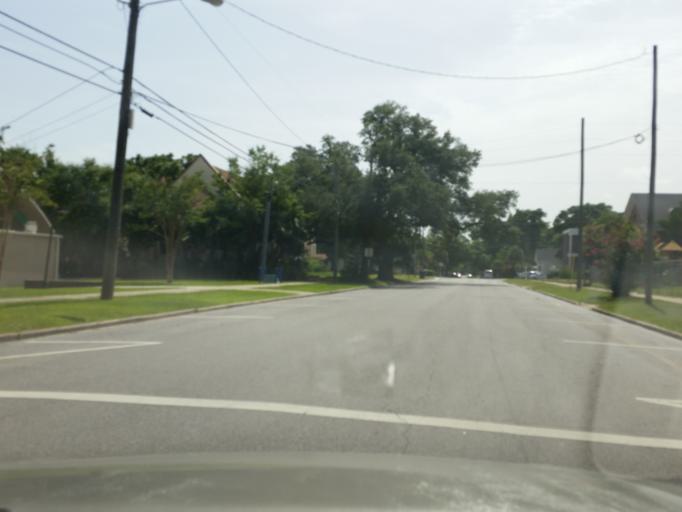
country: US
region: Florida
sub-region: Escambia County
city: Pensacola
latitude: 30.4215
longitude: -87.2053
